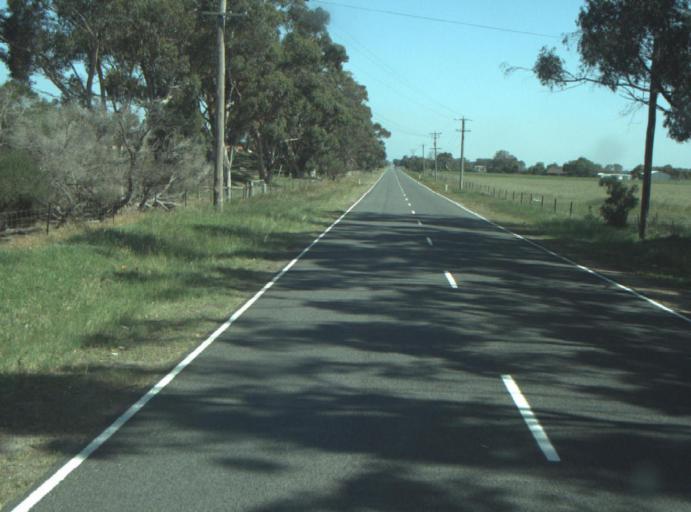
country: AU
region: Victoria
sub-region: Greater Geelong
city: Lara
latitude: -37.9720
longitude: 144.4055
